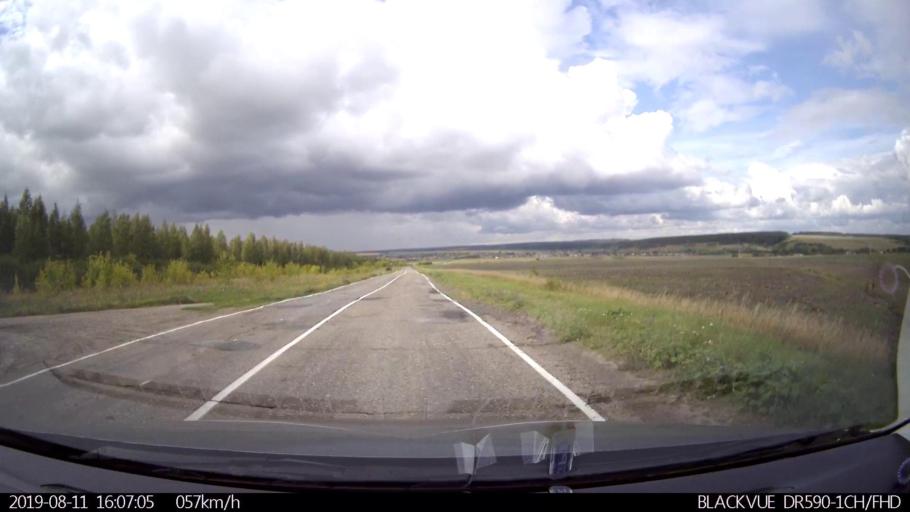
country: RU
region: Ulyanovsk
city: Ignatovka
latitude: 53.9745
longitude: 47.6459
